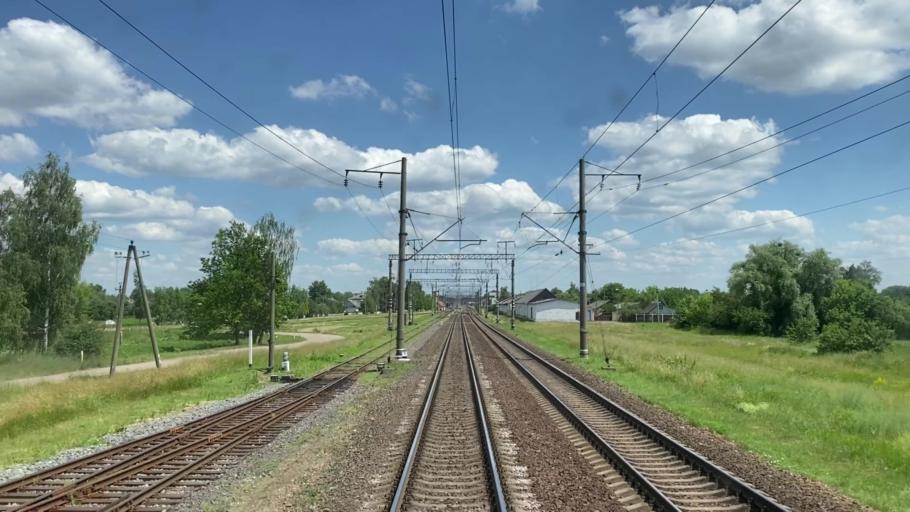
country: BY
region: Brest
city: Byaroza
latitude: 52.5308
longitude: 24.8881
